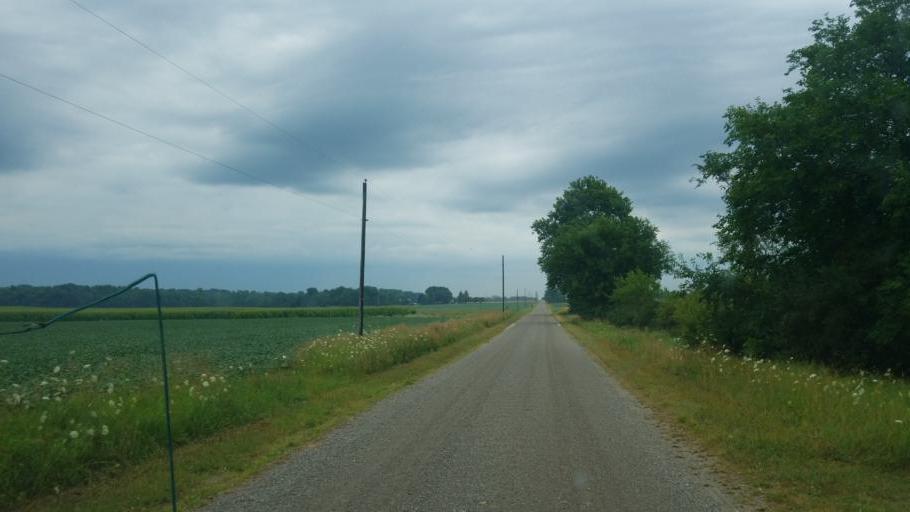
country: US
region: Indiana
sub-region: DeKalb County
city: Butler
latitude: 41.4429
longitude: -84.9040
